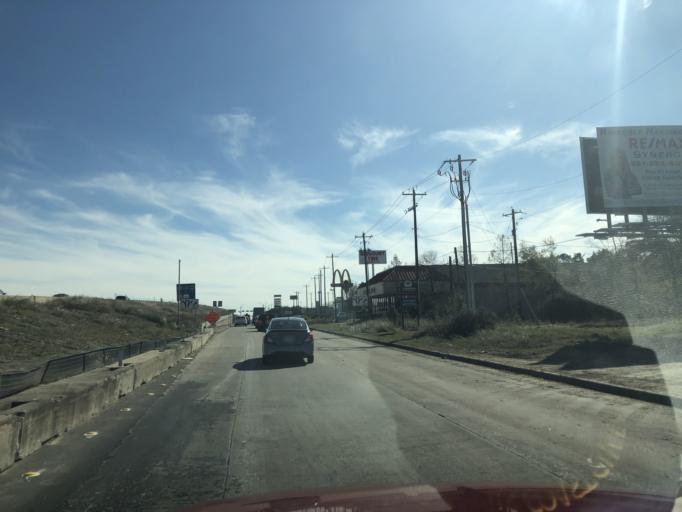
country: US
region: Texas
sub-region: Galveston County
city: League City
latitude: 29.5054
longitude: -95.1159
